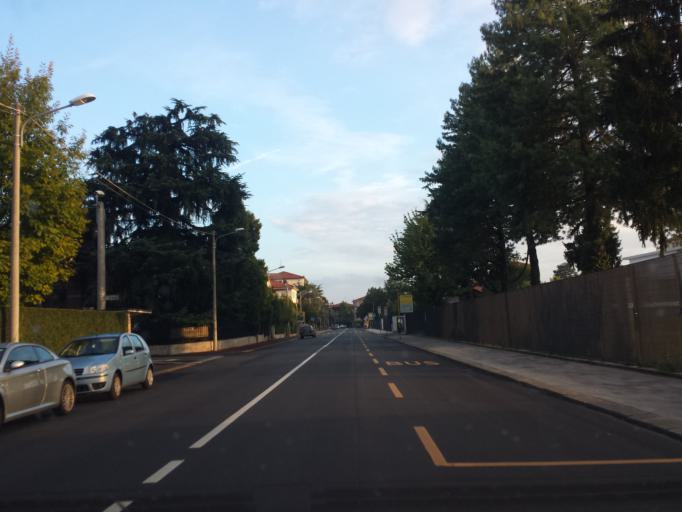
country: IT
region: Veneto
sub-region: Provincia di Vicenza
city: Vicenza
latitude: 45.5598
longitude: 11.5350
